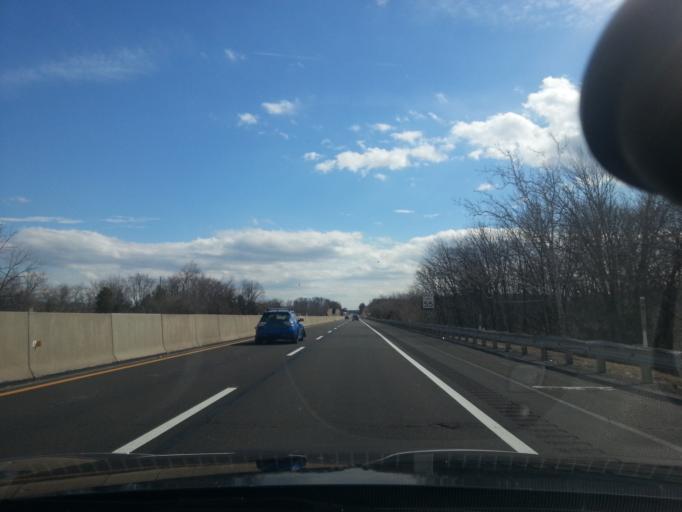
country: US
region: Pennsylvania
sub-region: Montgomery County
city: Harleysville
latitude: 40.3120
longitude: -75.3743
